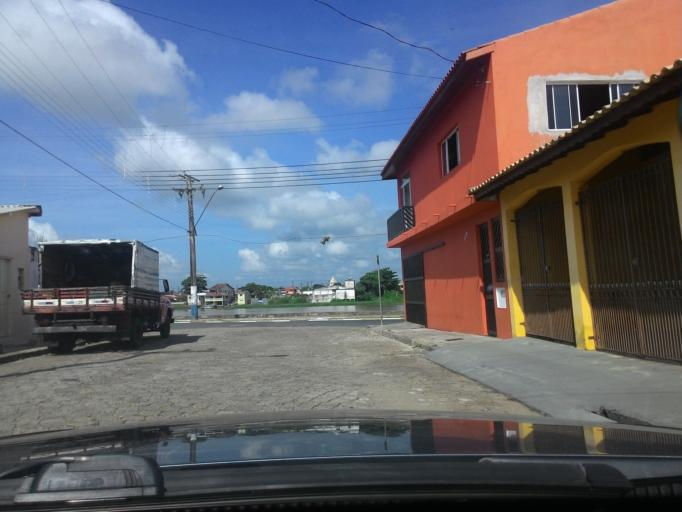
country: BR
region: Sao Paulo
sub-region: Iguape
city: Iguape
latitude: -24.7097
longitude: -47.5622
